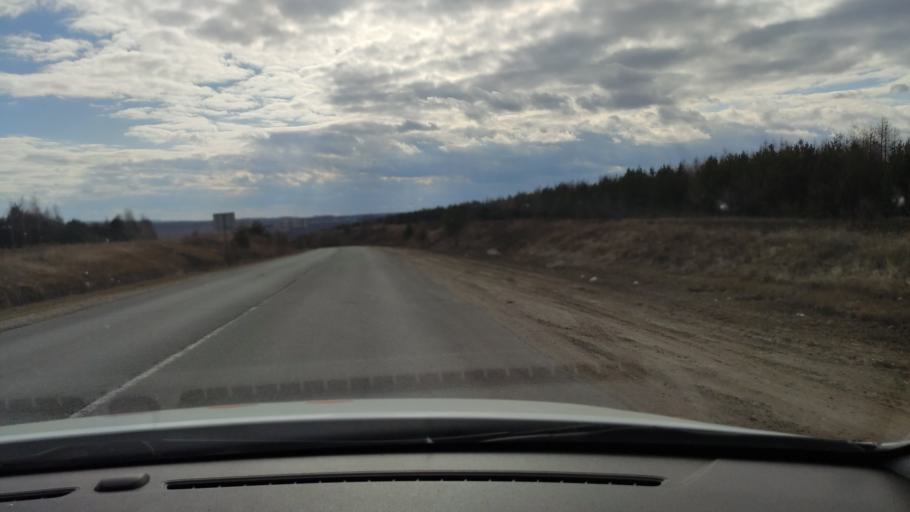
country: RU
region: Tatarstan
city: Vysokaya Gora
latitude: 56.0360
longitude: 49.2149
